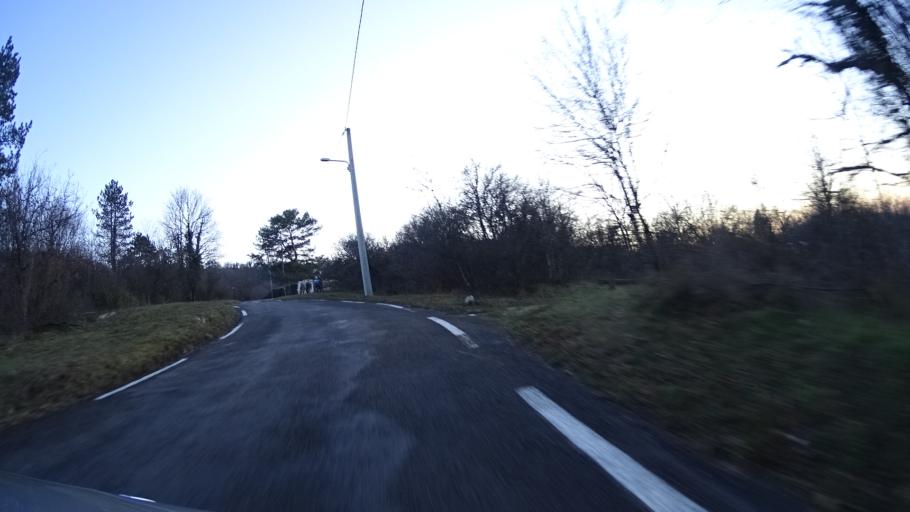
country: FR
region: Franche-Comte
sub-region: Departement du Doubs
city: Morre
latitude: 47.2211
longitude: 6.0416
